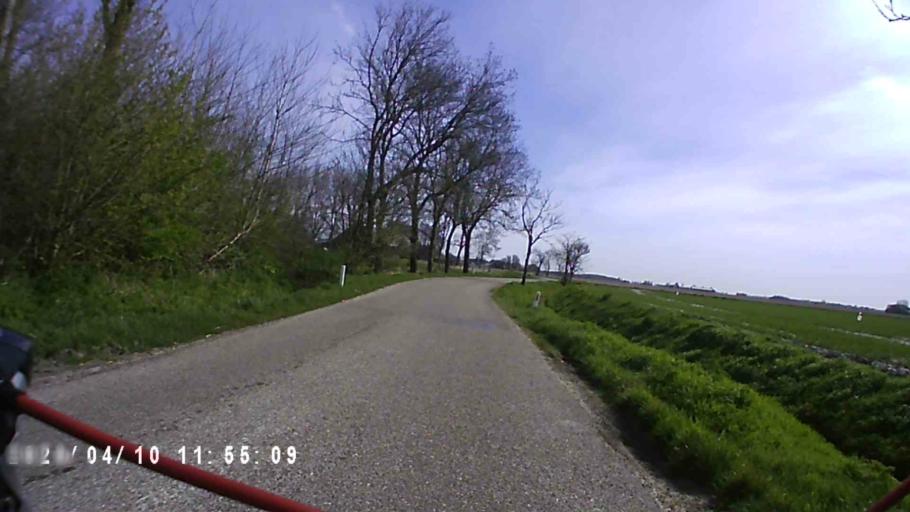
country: NL
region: Groningen
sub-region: Gemeente De Marne
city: Ulrum
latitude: 53.3858
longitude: 6.3404
